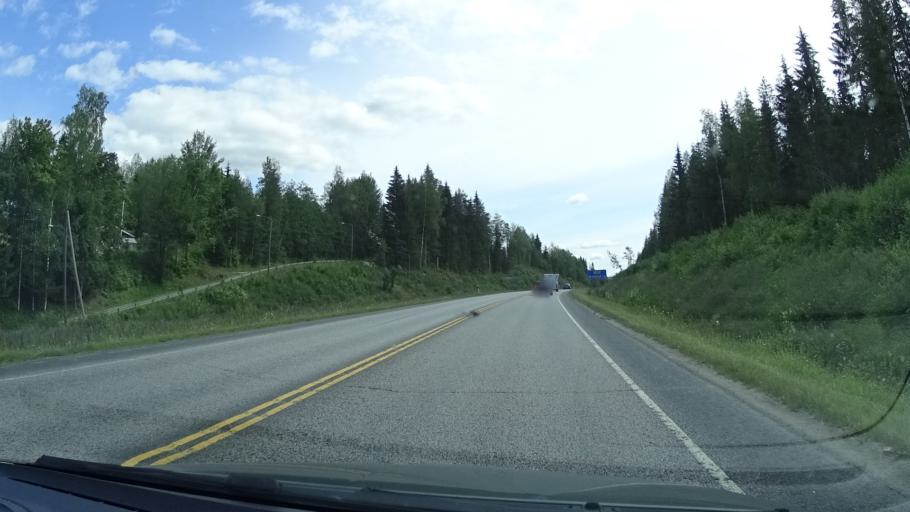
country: FI
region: Central Finland
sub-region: Jyvaeskylae
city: Jyvaeskylae
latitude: 62.2645
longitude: 25.5822
